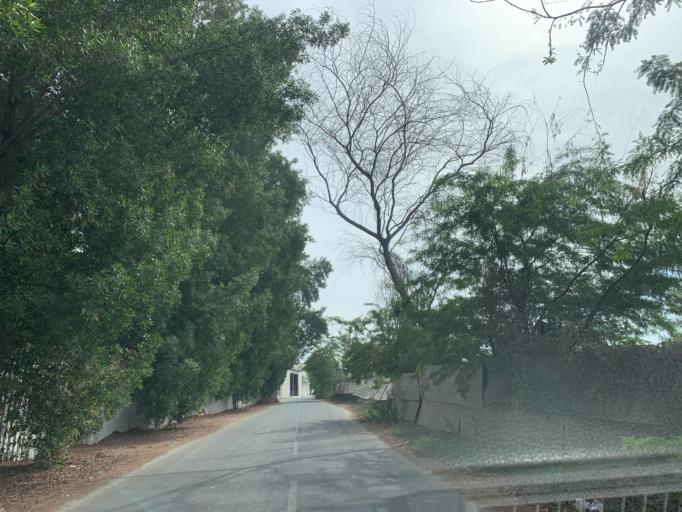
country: BH
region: Central Governorate
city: Madinat Hamad
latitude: 26.1149
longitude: 50.4721
